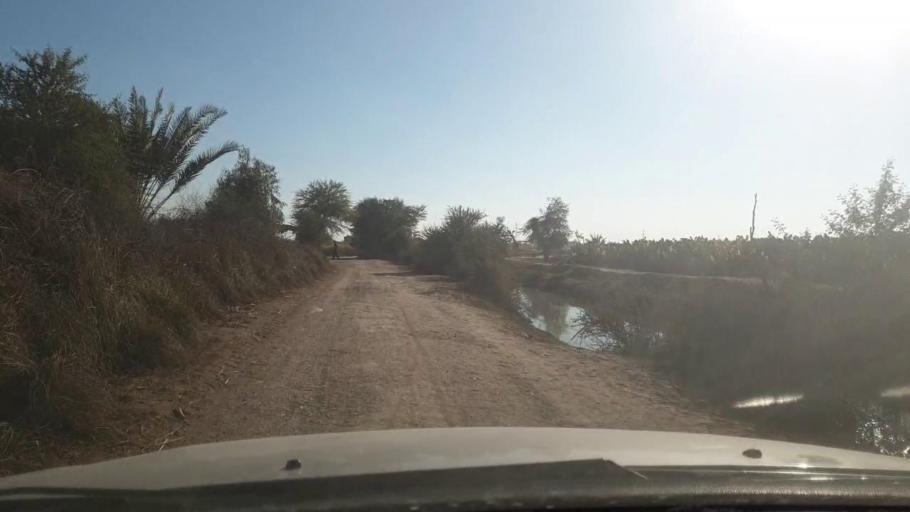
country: PK
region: Sindh
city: Adilpur
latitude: 27.9599
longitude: 69.2230
